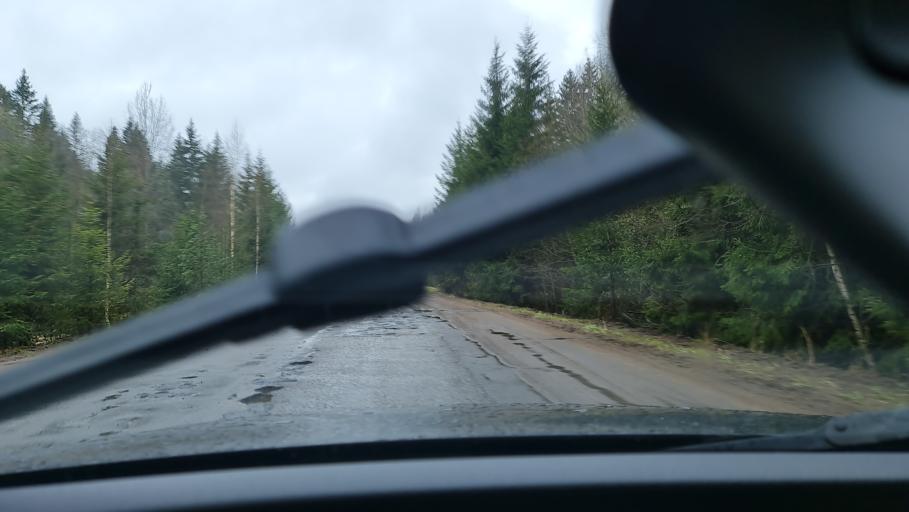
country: RU
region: Novgorod
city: Kresttsy
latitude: 58.0323
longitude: 32.8205
